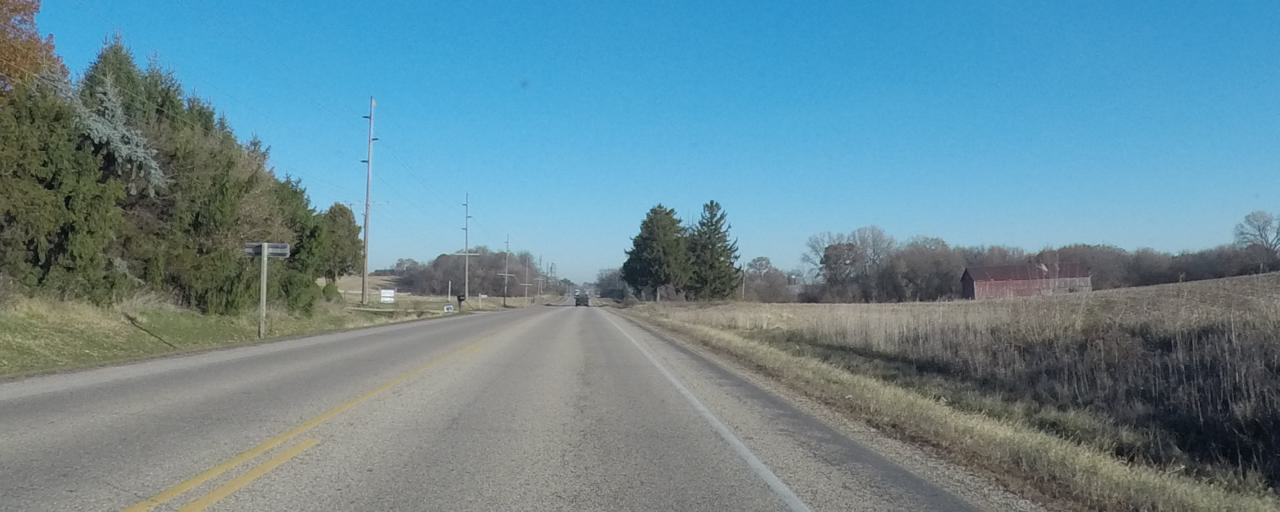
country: US
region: Wisconsin
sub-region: Dane County
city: Cottage Grove
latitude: 43.0511
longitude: -89.1999
